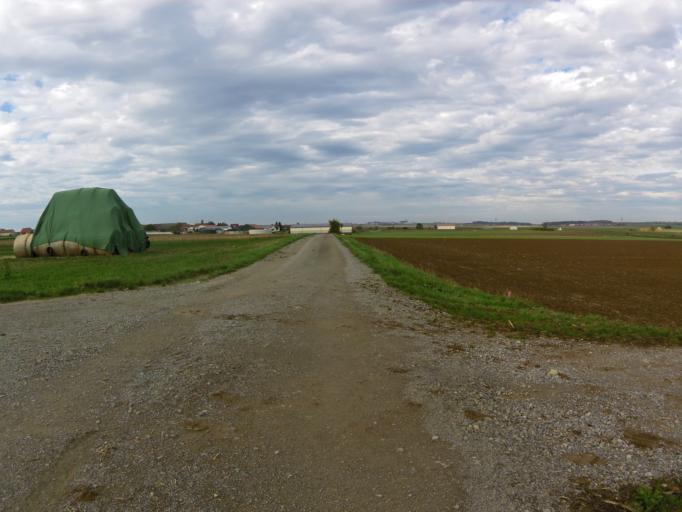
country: DE
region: Bavaria
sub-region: Regierungsbezirk Unterfranken
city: Biebelried
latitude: 49.7377
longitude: 10.0718
